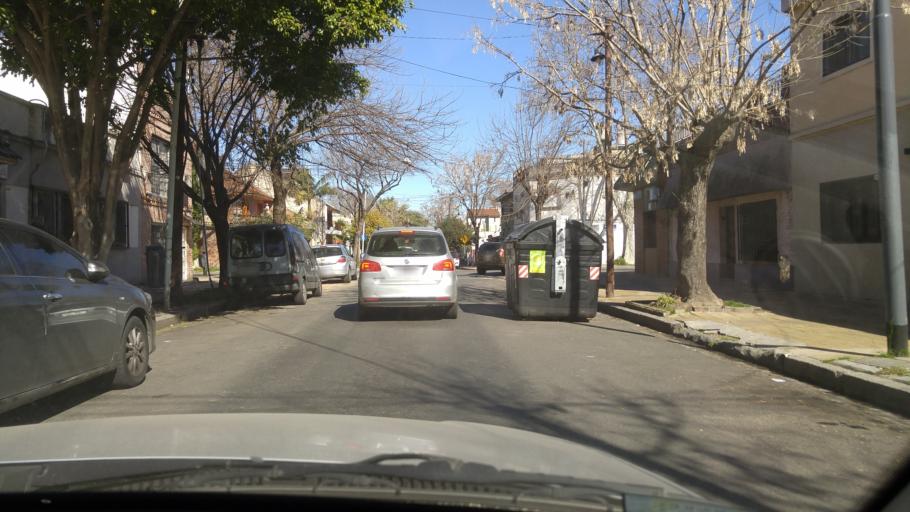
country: AR
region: Buenos Aires F.D.
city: Villa Santa Rita
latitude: -34.6304
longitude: -58.5050
